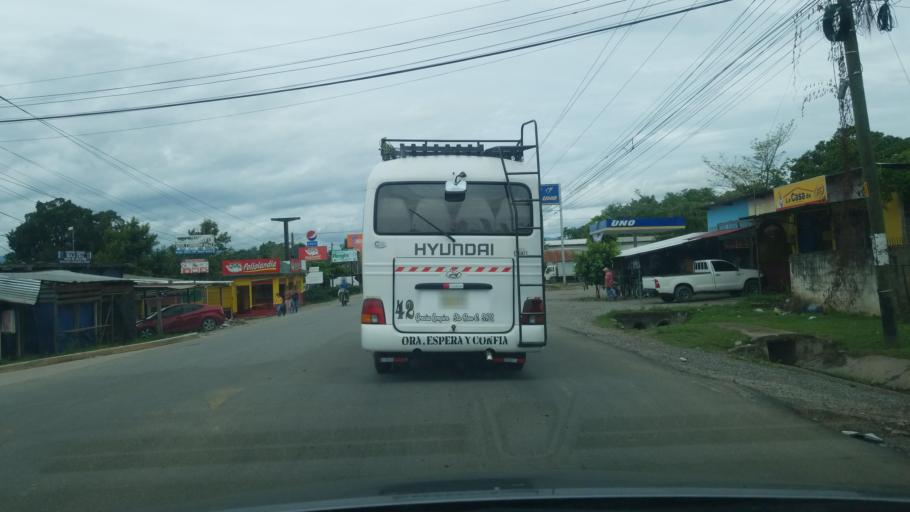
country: HN
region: Santa Barbara
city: El Ciruelo
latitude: 15.2935
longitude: -88.4909
